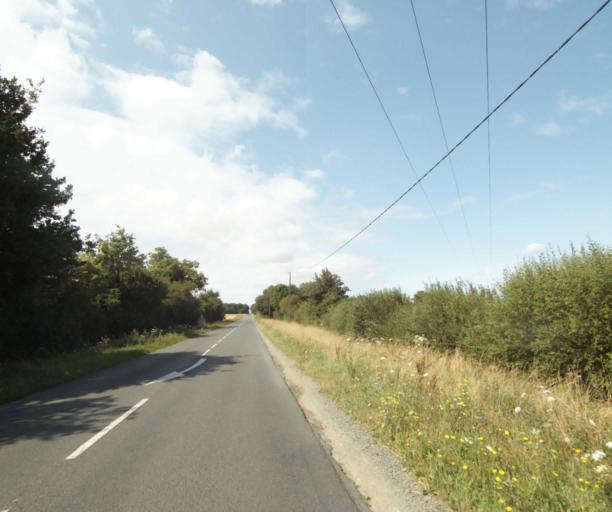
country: FR
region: Pays de la Loire
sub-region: Departement de la Sarthe
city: Sable-sur-Sarthe
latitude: 47.8365
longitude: -0.3655
